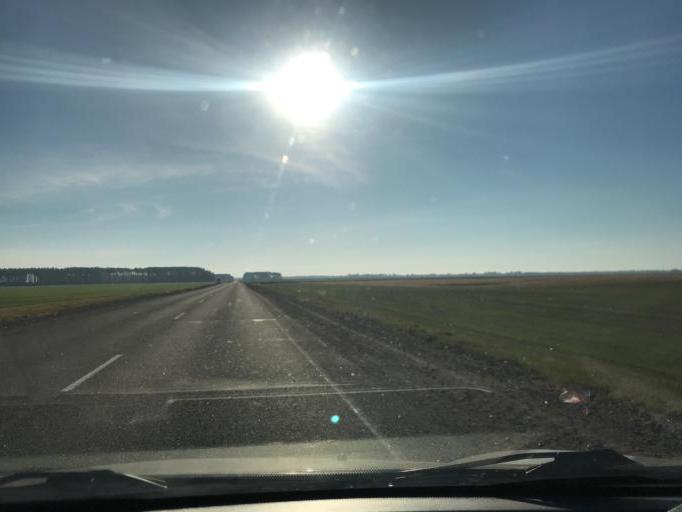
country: BY
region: Gomel
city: Khoyniki
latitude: 51.8231
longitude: 30.0755
